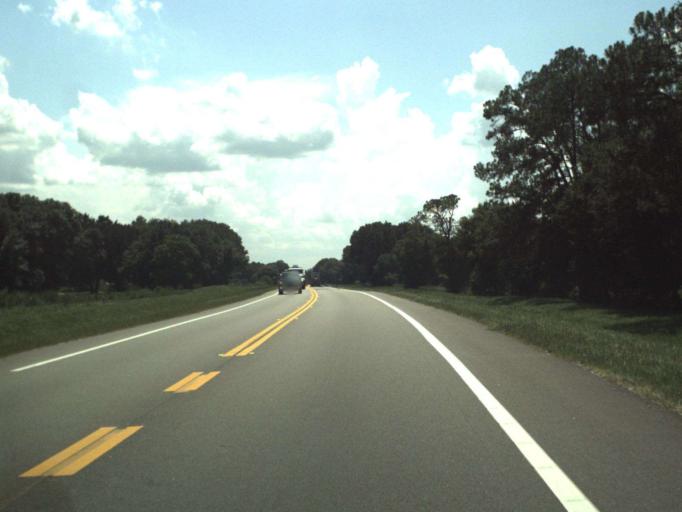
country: US
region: Florida
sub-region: Lake County
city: Mascotte
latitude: 28.5803
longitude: -81.9738
